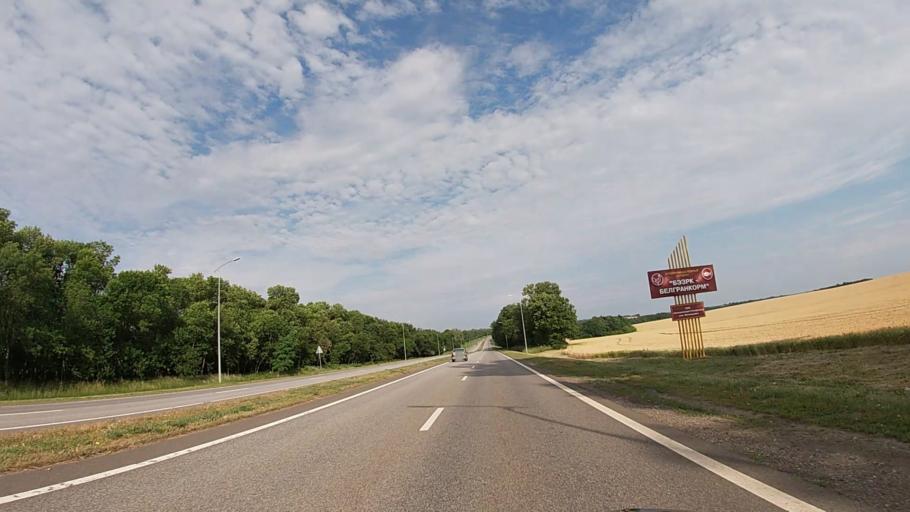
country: RU
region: Belgorod
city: Tomarovka
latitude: 50.6647
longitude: 36.3232
